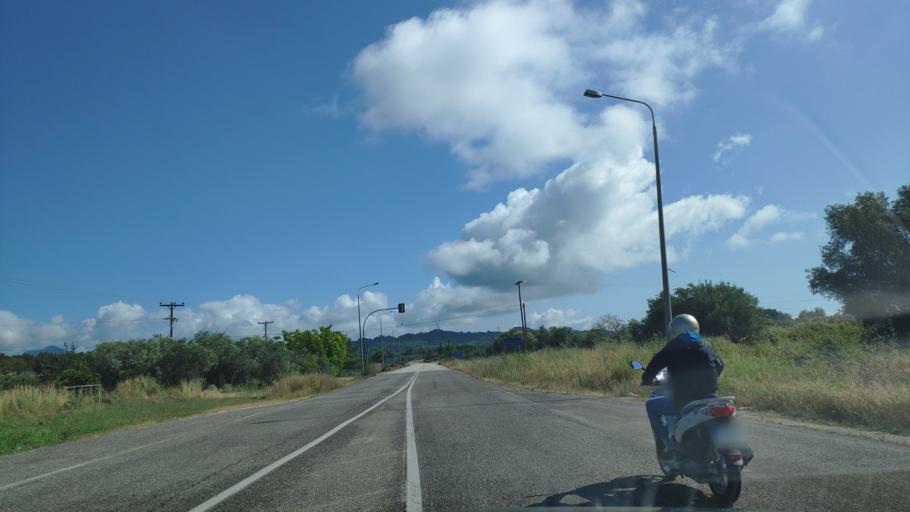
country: GR
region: Epirus
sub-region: Nomos Prevezis
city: Preveza
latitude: 39.0031
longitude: 20.7176
